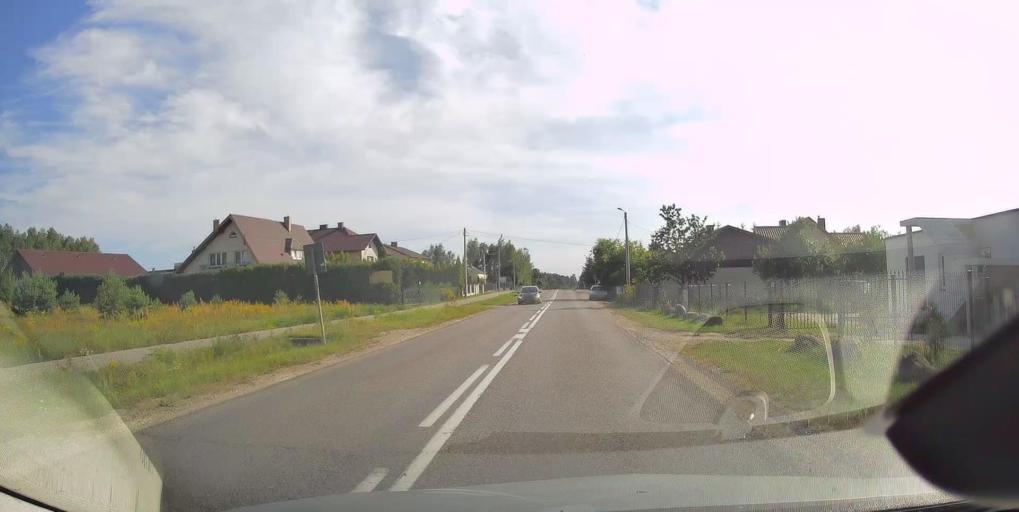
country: PL
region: Swietokrzyskie
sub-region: Powiat konecki
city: Radoszyce
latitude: 51.0842
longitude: 20.2869
